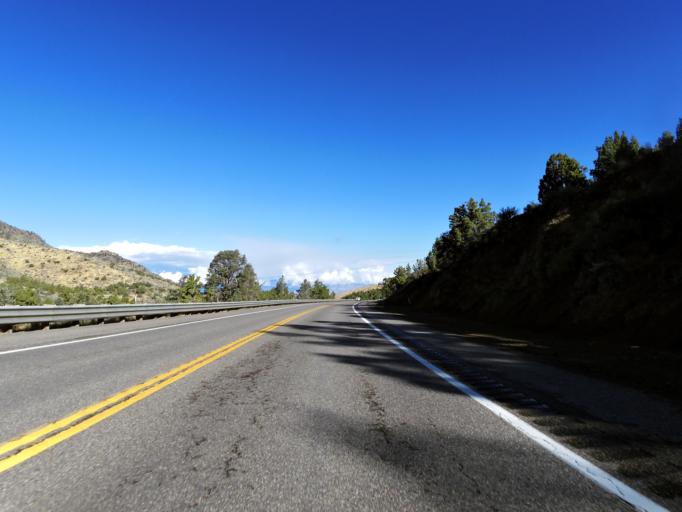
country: US
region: Nevada
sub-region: Douglas County
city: Gardnerville Ranchos
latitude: 38.8319
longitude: -119.6302
